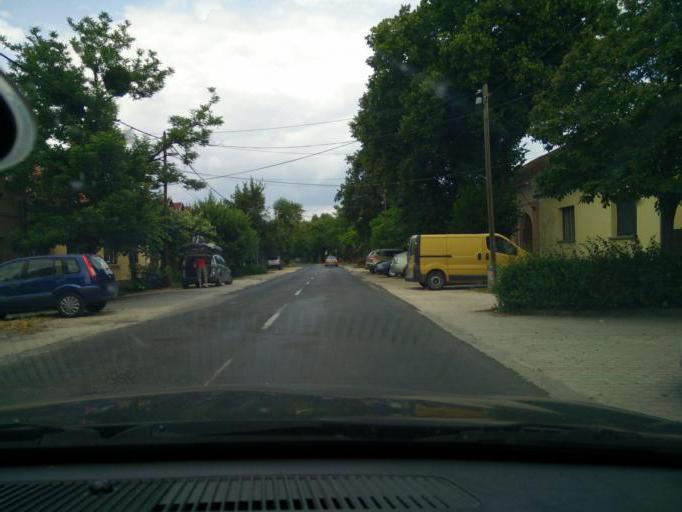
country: HU
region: Komarom-Esztergom
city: Tata
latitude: 47.6538
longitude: 18.3284
